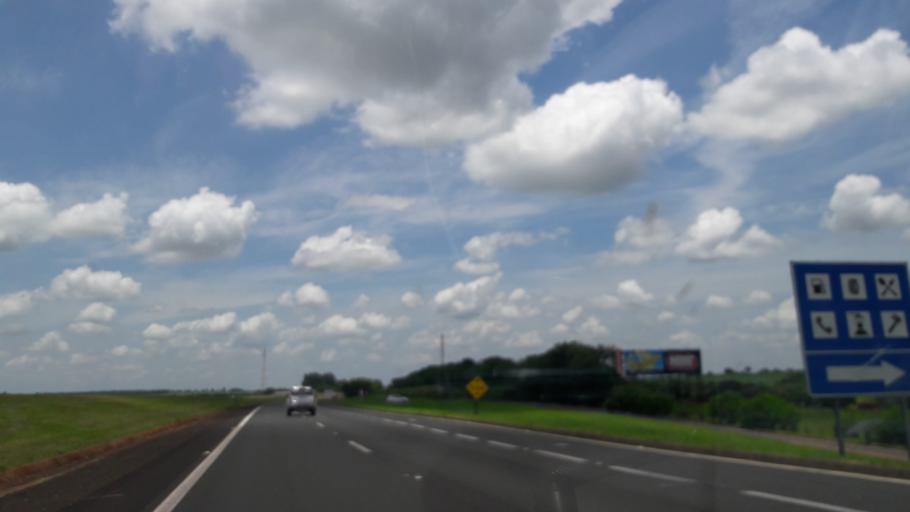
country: BR
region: Sao Paulo
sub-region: Avare
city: Avare
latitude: -22.9571
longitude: -48.8520
